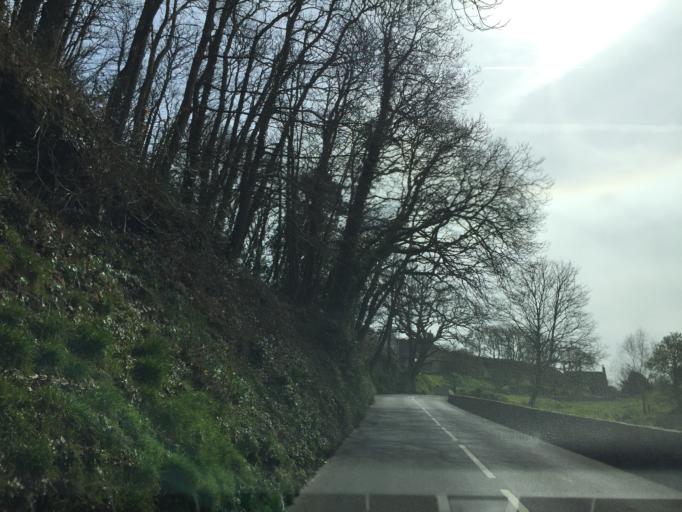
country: JE
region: St Helier
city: Saint Helier
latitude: 49.2430
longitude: -2.2035
